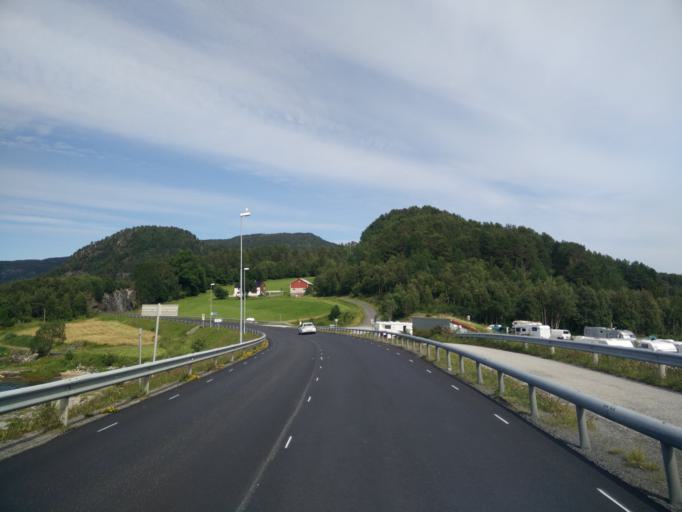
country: NO
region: More og Romsdal
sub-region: Kristiansund
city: Rensvik
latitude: 62.9892
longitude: 7.8806
